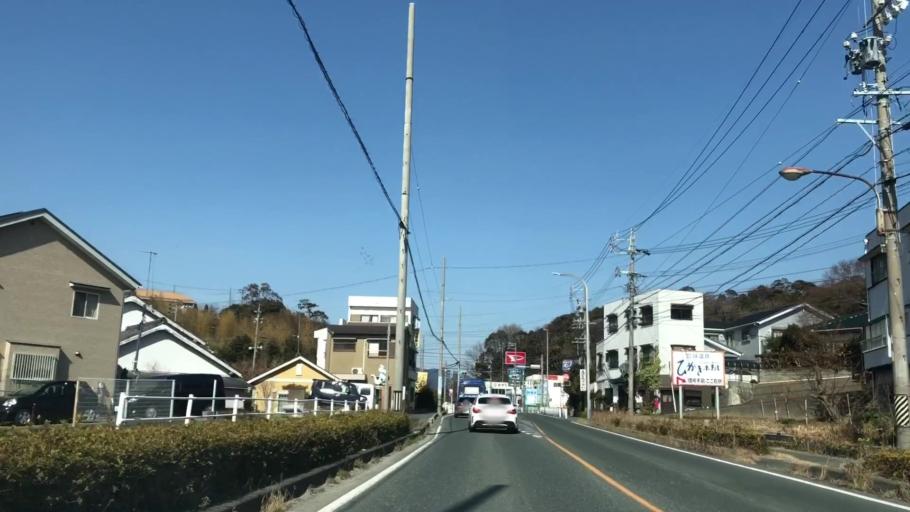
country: JP
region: Aichi
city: Gamagori
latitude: 34.8072
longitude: 137.2587
